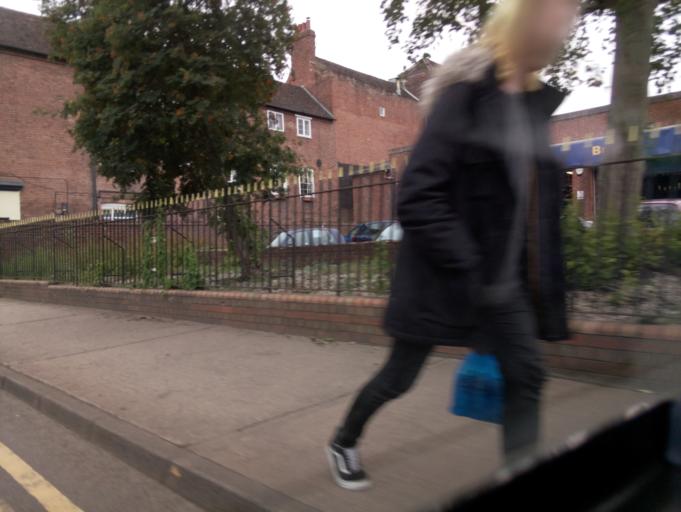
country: GB
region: England
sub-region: Worcestershire
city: Worcester
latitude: 52.2018
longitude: -2.2256
